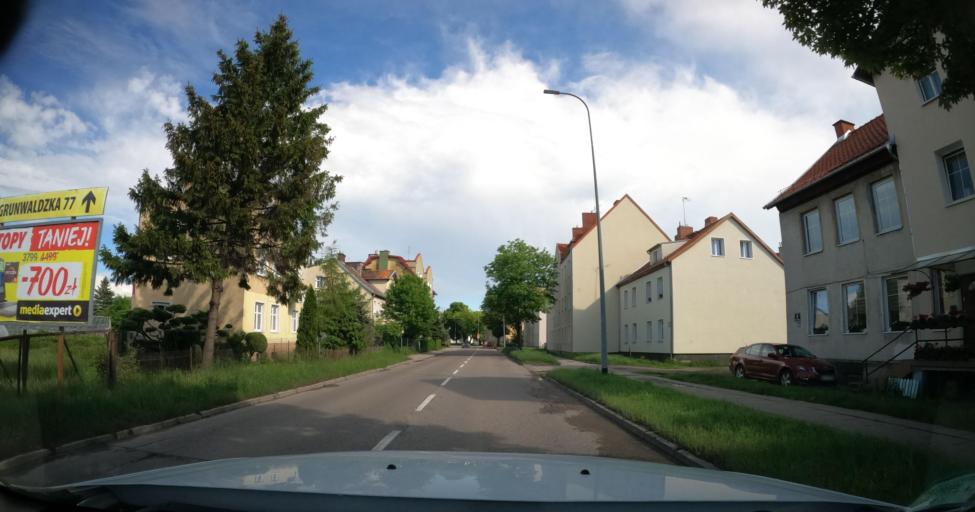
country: PL
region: Warmian-Masurian Voivodeship
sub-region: Powiat elblaski
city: Elblag
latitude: 54.1612
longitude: 19.3839
